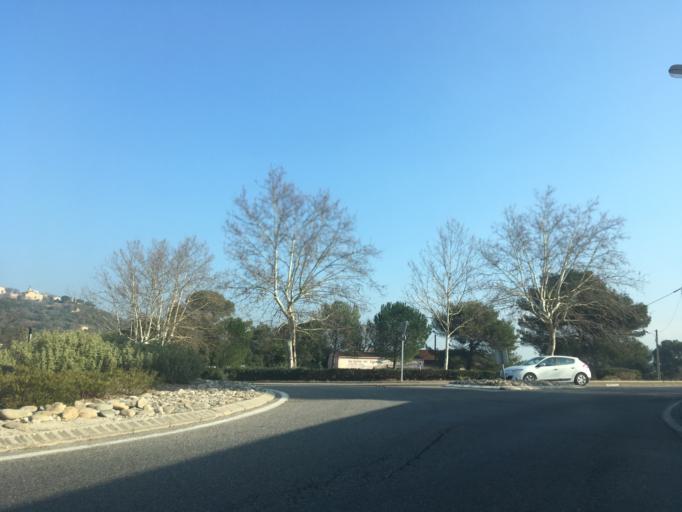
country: FR
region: Provence-Alpes-Cote d'Azur
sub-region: Departement du Var
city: Le Cannet-des-Maures
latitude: 43.3919
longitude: 6.3433
